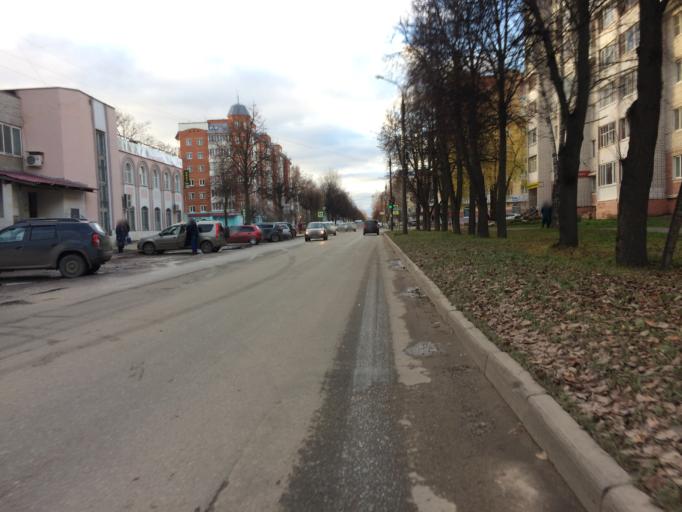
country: RU
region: Mariy-El
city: Yoshkar-Ola
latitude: 56.6441
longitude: 47.9003
